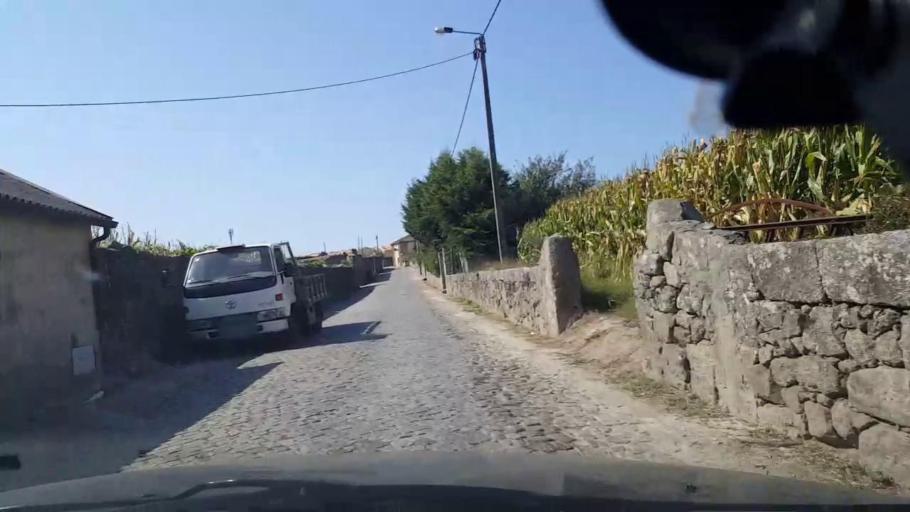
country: PT
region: Porto
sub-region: Vila do Conde
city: Arvore
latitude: 41.3744
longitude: -8.7123
